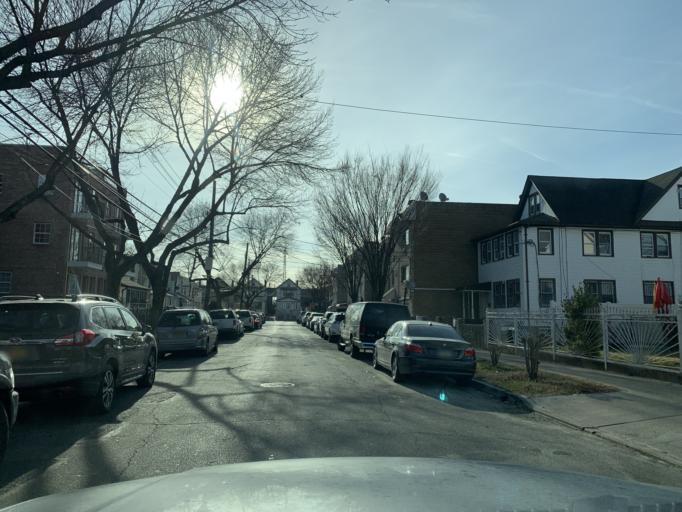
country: US
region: New York
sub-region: Queens County
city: Jamaica
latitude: 40.7072
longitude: -73.7865
